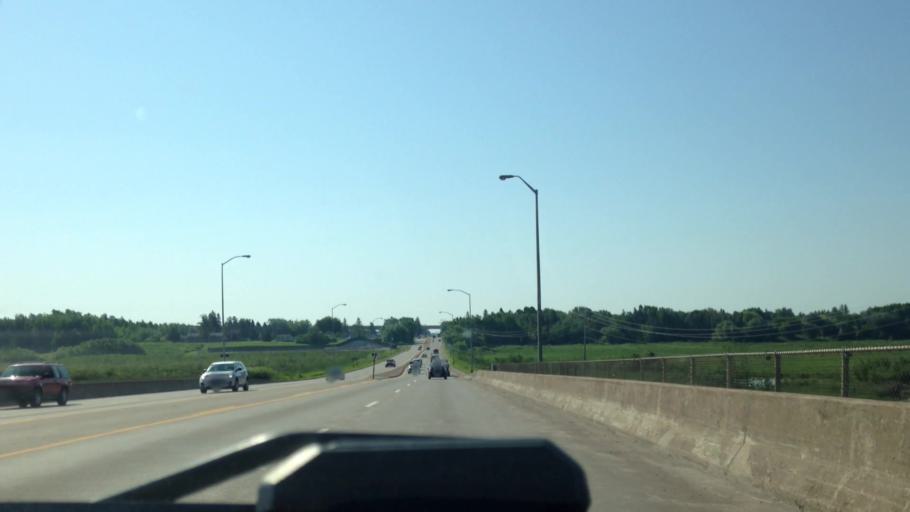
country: US
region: Wisconsin
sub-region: Douglas County
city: Superior
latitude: 46.6972
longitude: -92.0356
